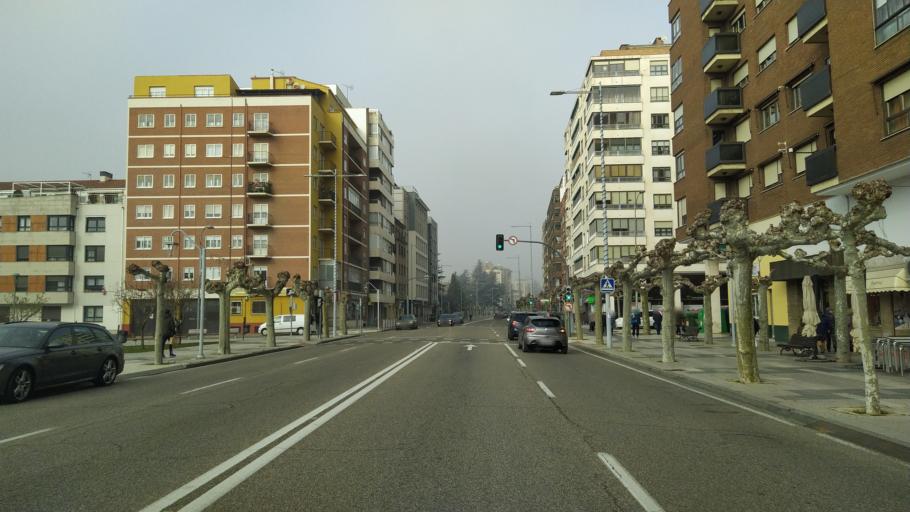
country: ES
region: Castille and Leon
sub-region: Provincia de Palencia
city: Palencia
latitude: 41.9996
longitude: -4.5250
